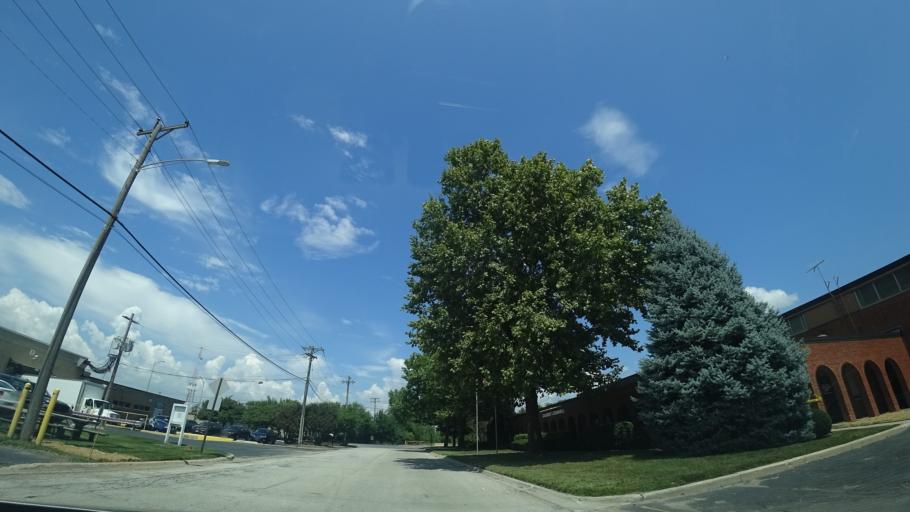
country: US
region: Illinois
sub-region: Cook County
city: Robbins
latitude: 41.6614
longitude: -87.7128
